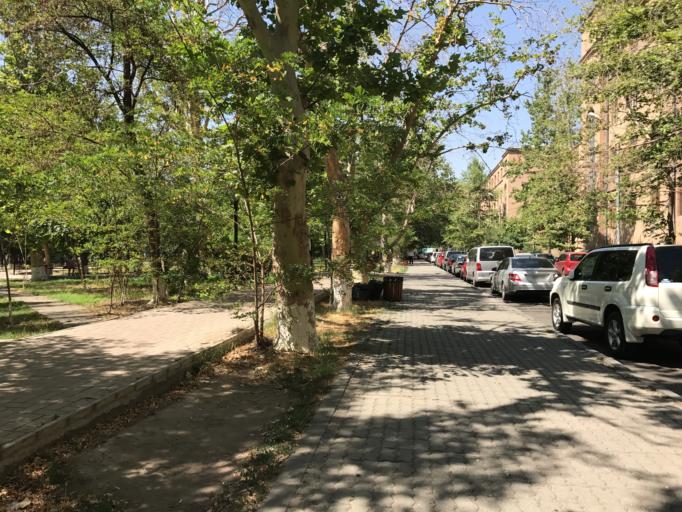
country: AM
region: Yerevan
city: Yerevan
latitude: 40.1866
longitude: 44.5165
